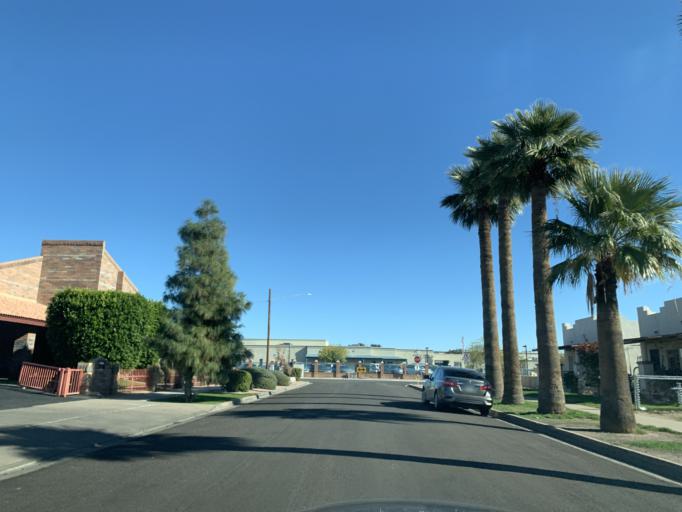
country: US
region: Arizona
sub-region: Maricopa County
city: Phoenix
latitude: 33.4494
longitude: -112.0549
